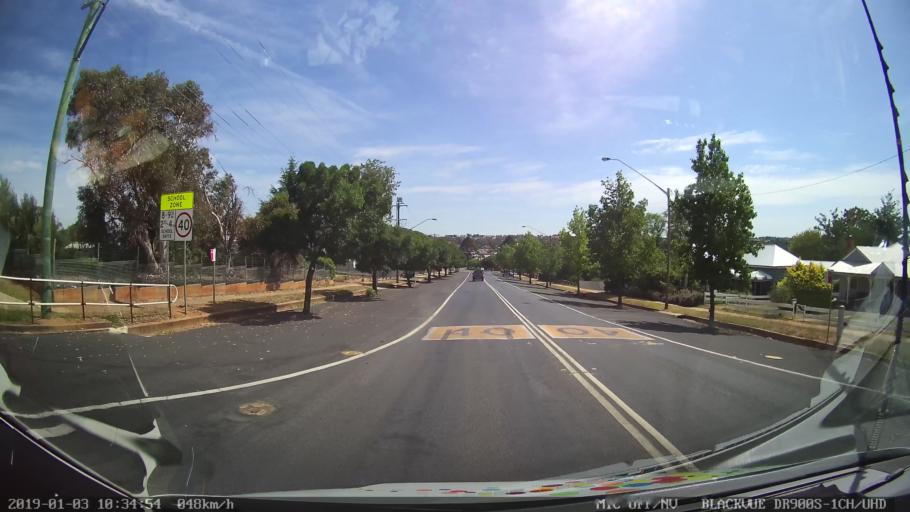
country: AU
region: New South Wales
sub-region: Young
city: Young
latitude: -34.3187
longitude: 148.2926
